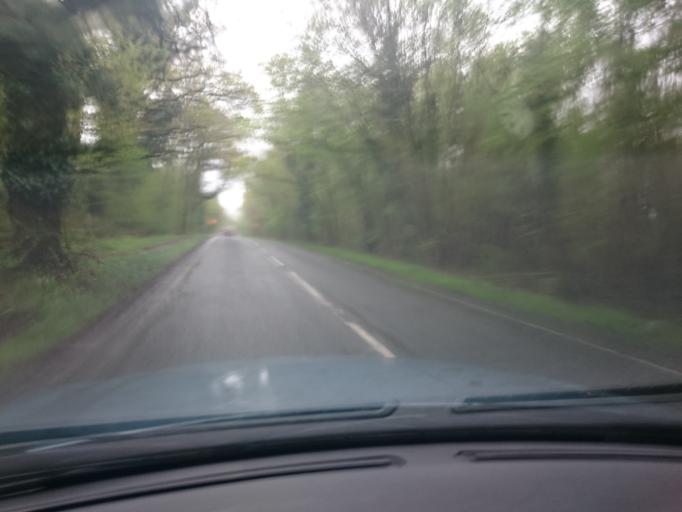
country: GB
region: England
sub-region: Hampshire
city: Lindford
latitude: 51.1013
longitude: -0.8362
